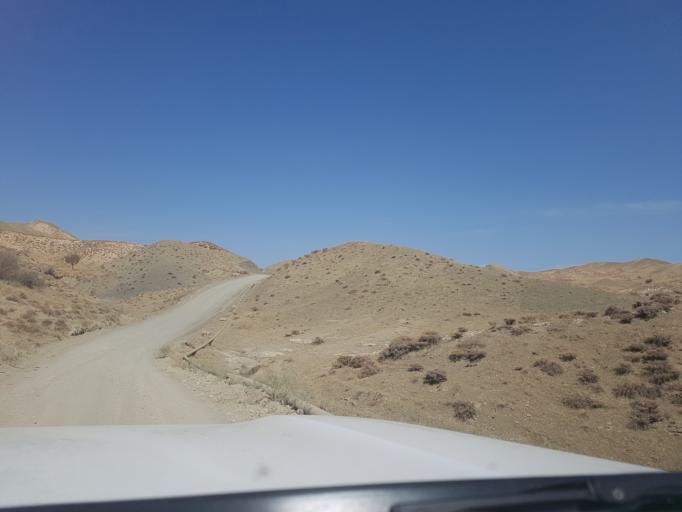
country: TM
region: Ahal
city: Baharly
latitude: 38.2506
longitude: 56.8911
